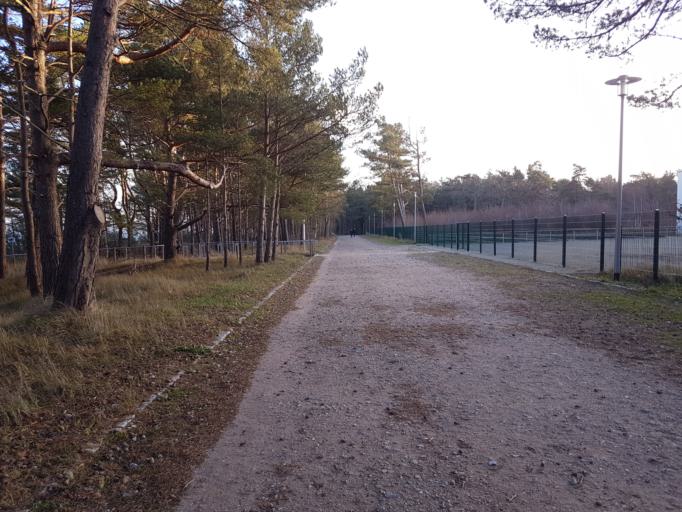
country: DE
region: Mecklenburg-Vorpommern
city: Ostseebad Binz
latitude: 54.4283
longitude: 13.5843
